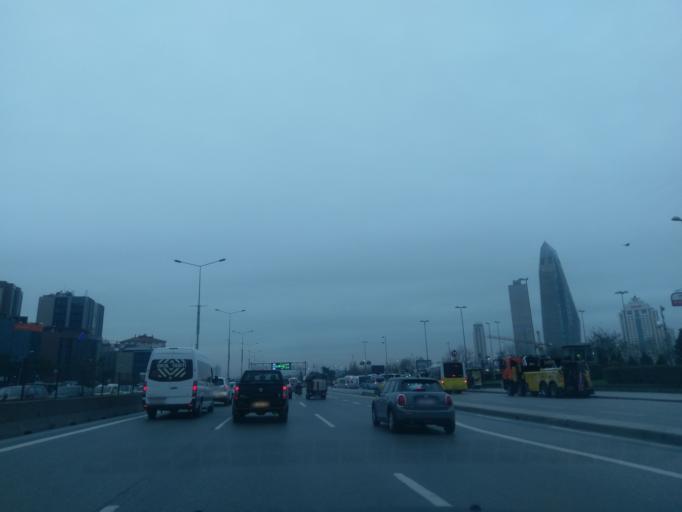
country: TR
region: Istanbul
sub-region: Atasehir
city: Atasehir
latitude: 40.9745
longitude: 29.0996
